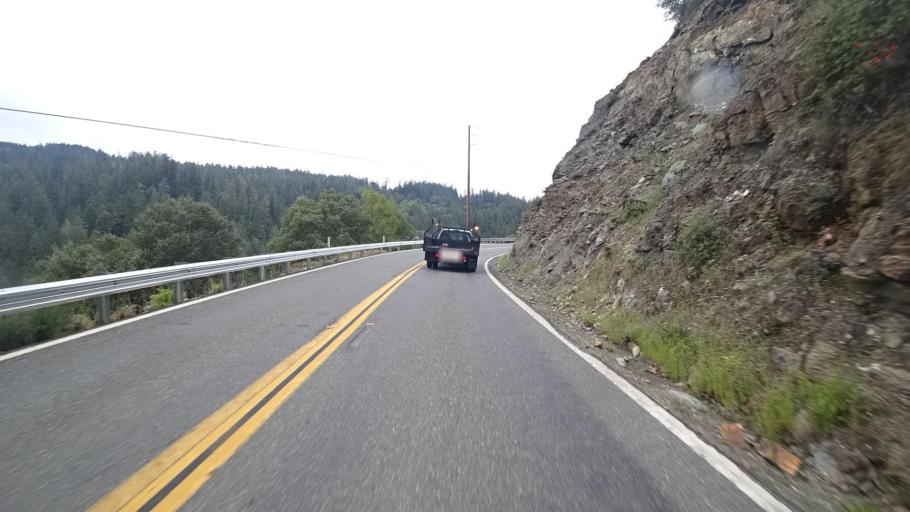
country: US
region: California
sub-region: Humboldt County
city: Willow Creek
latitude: 41.1193
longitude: -123.6885
